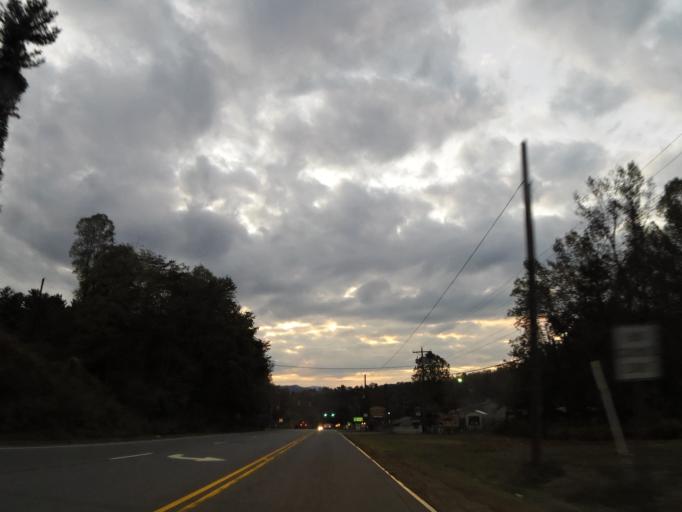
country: US
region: North Carolina
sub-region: Madison County
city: Marshall
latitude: 35.8142
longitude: -82.6774
